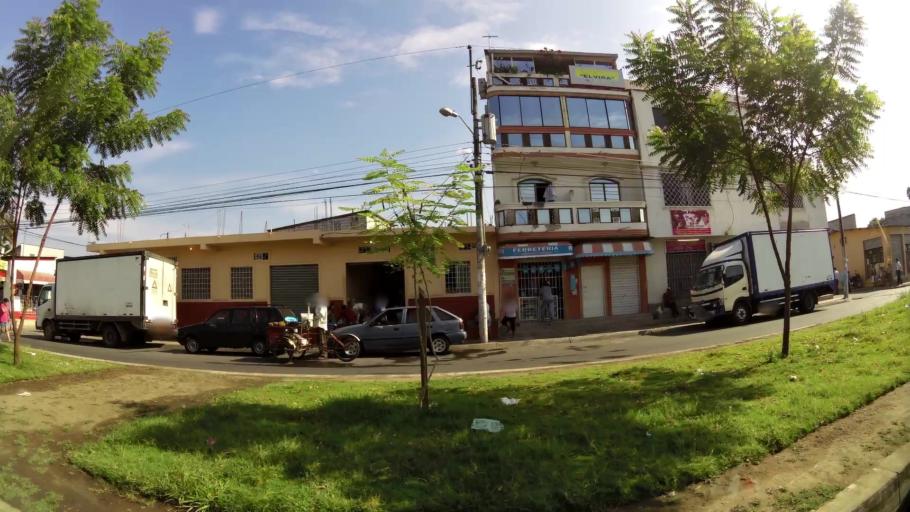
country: EC
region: Guayas
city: Eloy Alfaro
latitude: -2.0870
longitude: -79.9184
